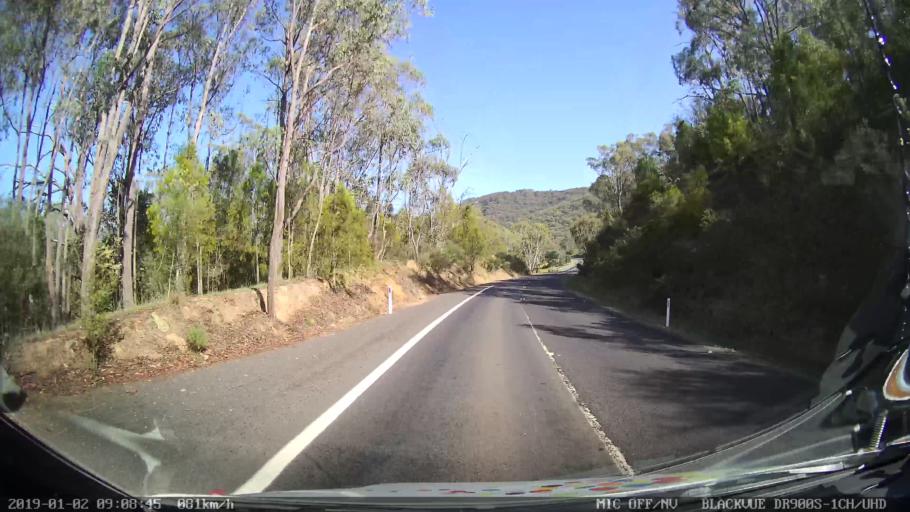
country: AU
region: New South Wales
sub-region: Tumut Shire
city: Tumut
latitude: -35.5293
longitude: 148.2871
